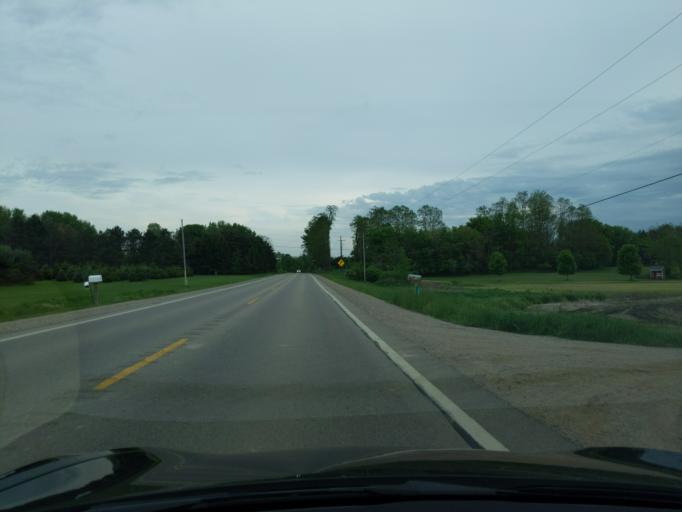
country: US
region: Michigan
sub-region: Jackson County
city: Michigan Center
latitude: 42.3682
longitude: -84.3251
